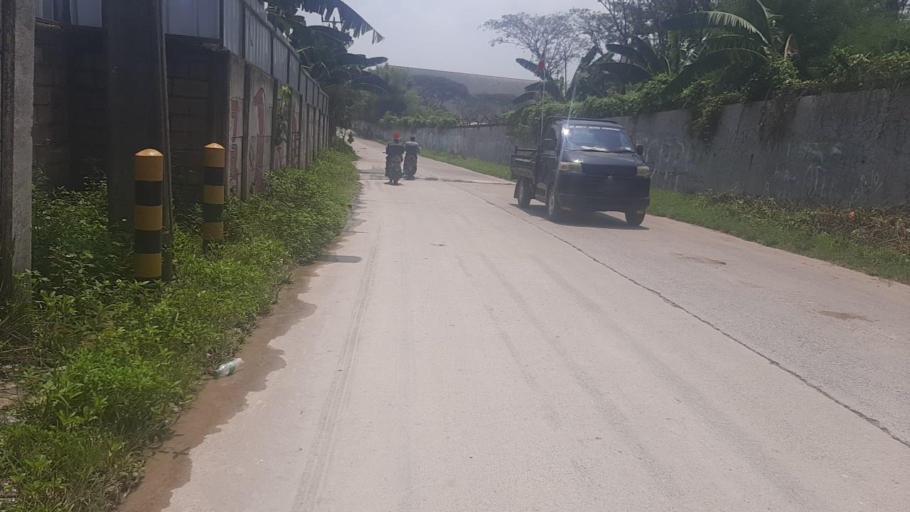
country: ID
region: West Java
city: Citeureup
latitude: -6.4649
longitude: 106.9306
